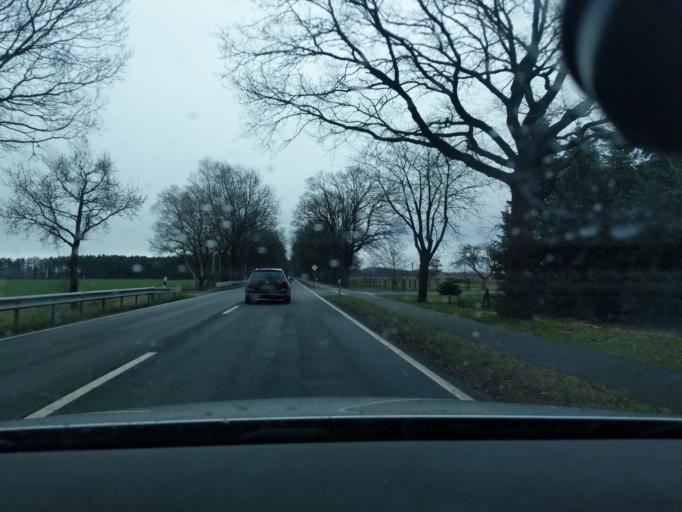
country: DE
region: Lower Saxony
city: Dudenbuttel
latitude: 53.5559
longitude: 9.3599
